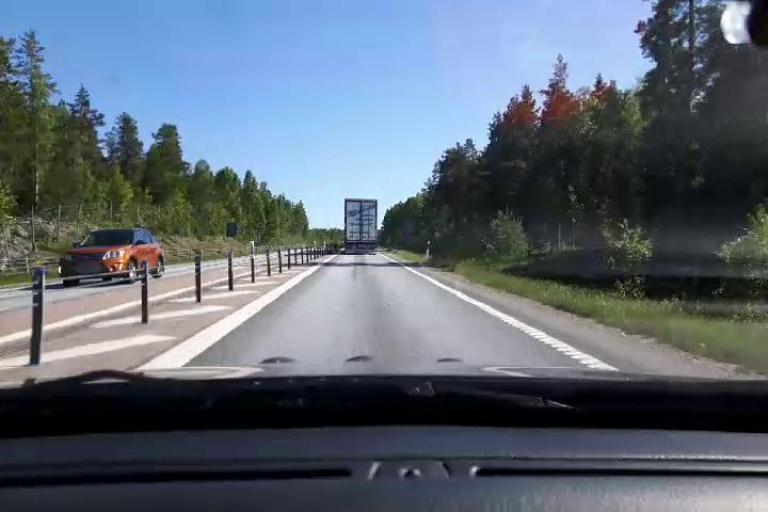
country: SE
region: Gaevleborg
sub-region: Soderhamns Kommun
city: Soderhamn
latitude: 61.2631
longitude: 17.0318
